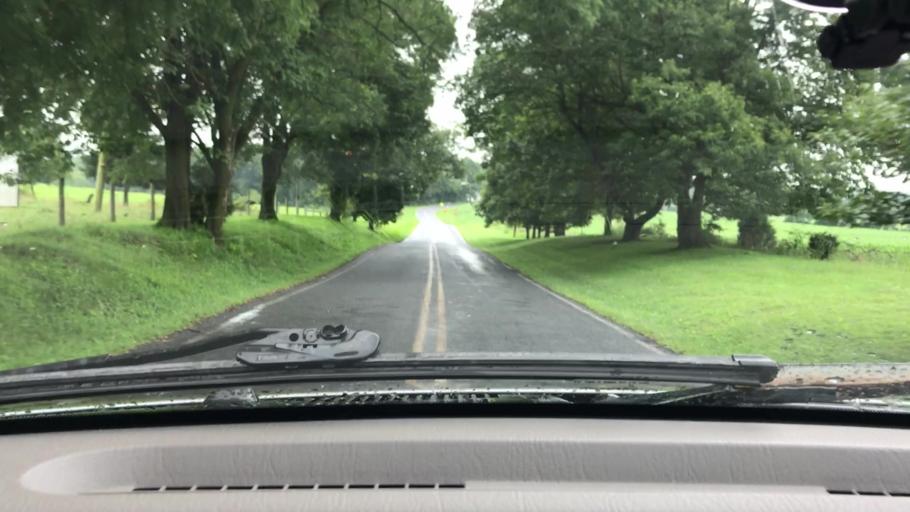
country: US
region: Pennsylvania
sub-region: Lancaster County
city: Elizabethtown
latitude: 40.2077
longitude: -76.6186
